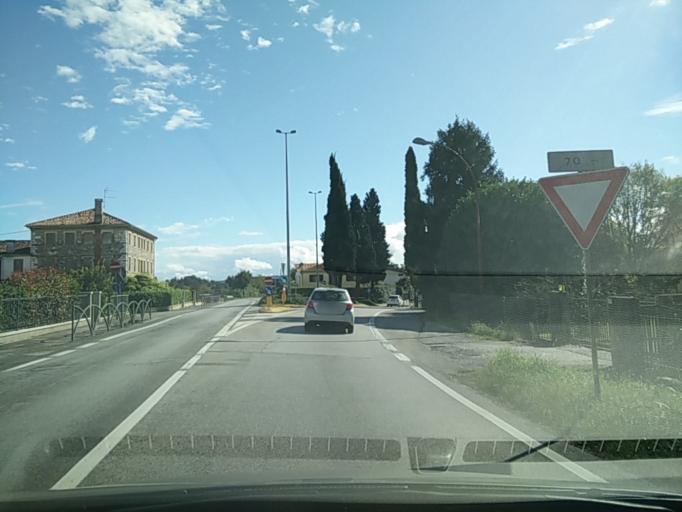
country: IT
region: Veneto
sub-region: Provincia di Treviso
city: Bigolino
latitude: 45.8640
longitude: 12.0219
